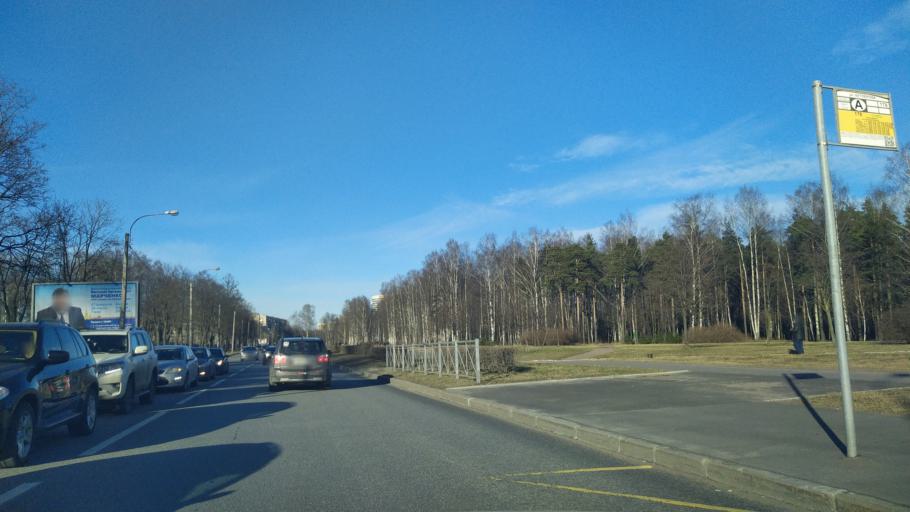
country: RU
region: Leningrad
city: Kalininskiy
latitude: 59.9950
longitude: 30.3916
